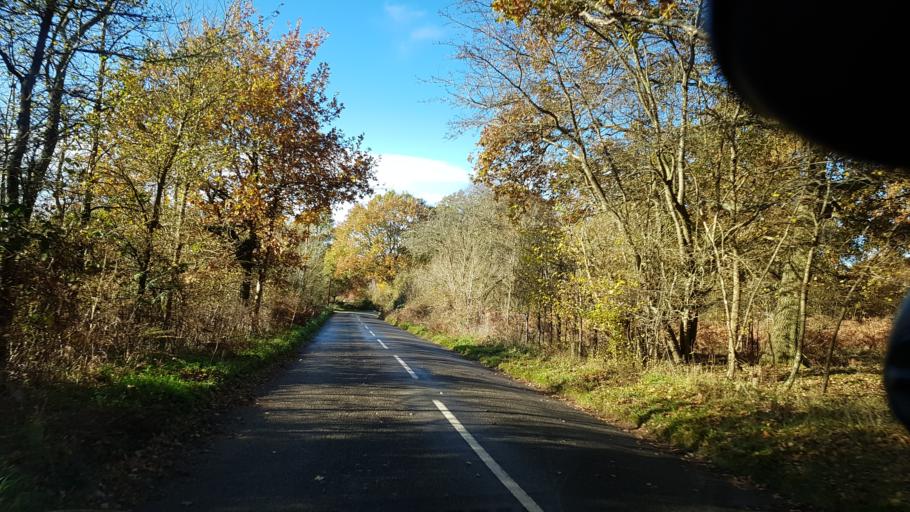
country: GB
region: England
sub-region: Surrey
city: Elstead
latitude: 51.2061
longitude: -0.6851
